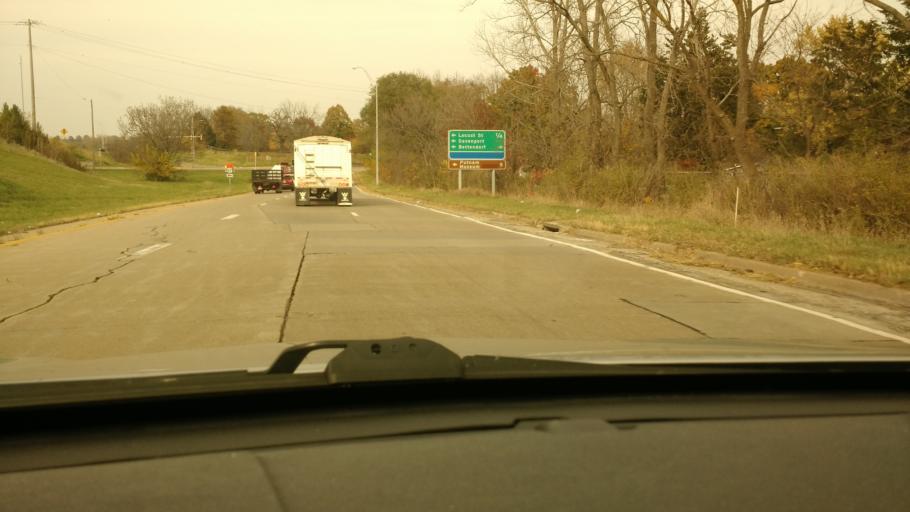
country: US
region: Iowa
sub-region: Scott County
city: Bettendorf
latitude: 41.5399
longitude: -90.5171
